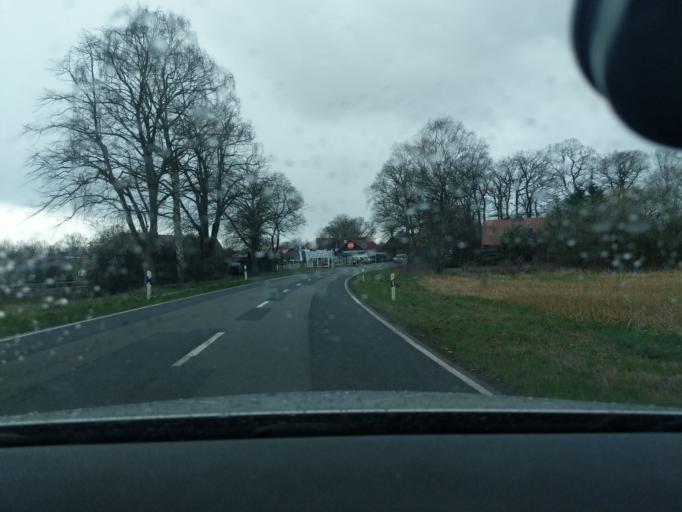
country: DE
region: Lower Saxony
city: Bargstedt
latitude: 53.4598
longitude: 9.4549
